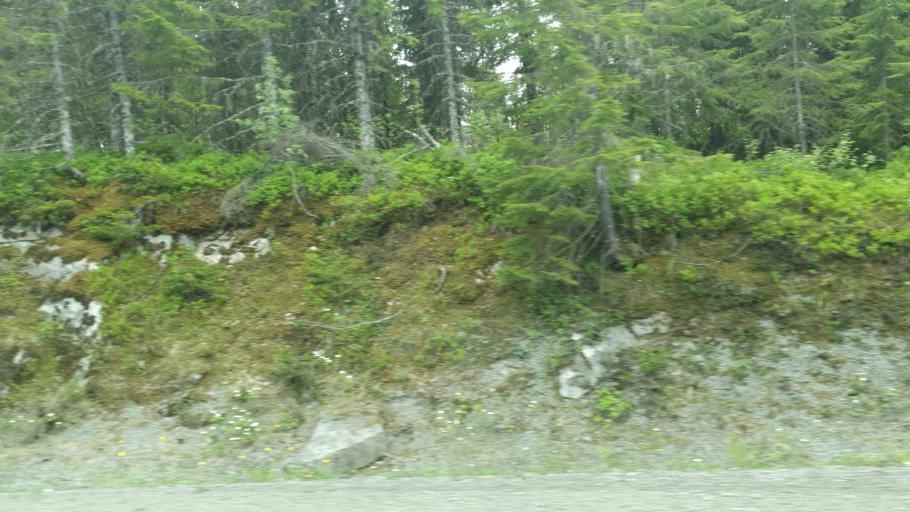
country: NO
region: Nord-Trondelag
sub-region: Leksvik
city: Leksvik
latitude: 63.6880
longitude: 10.4024
